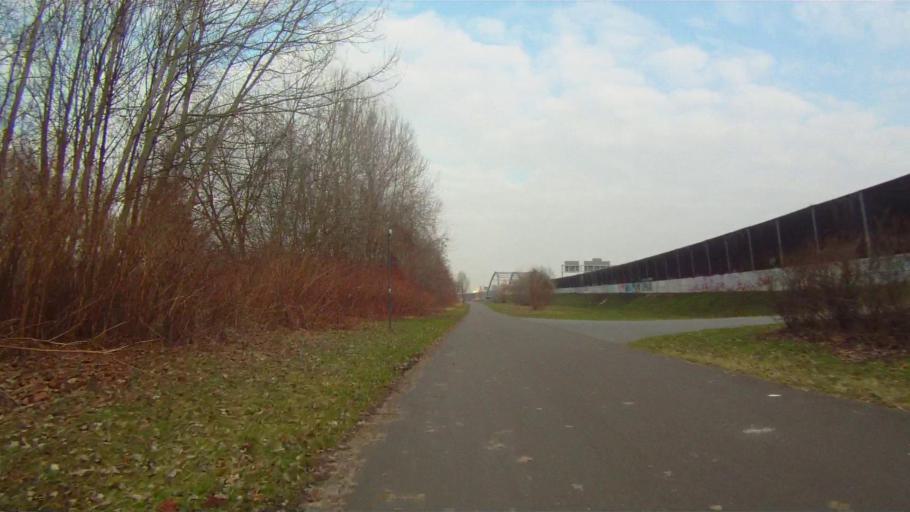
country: DE
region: Berlin
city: Buckow
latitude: 52.4556
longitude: 13.4600
